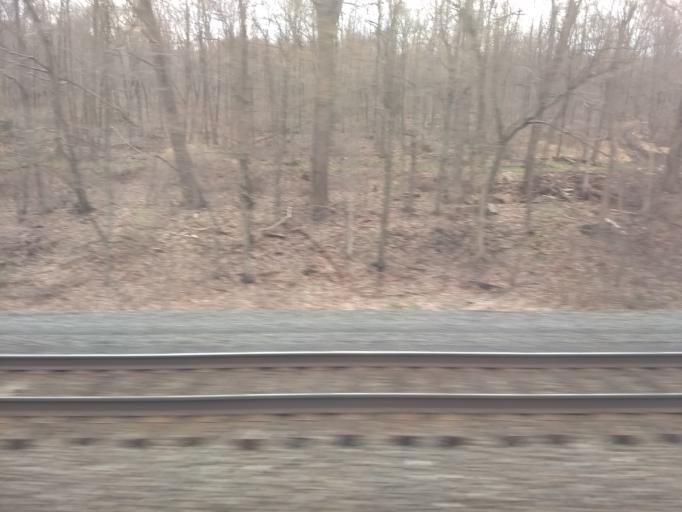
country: US
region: Pennsylvania
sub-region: Mifflin County
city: Belleville
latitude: 40.5097
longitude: -77.7153
